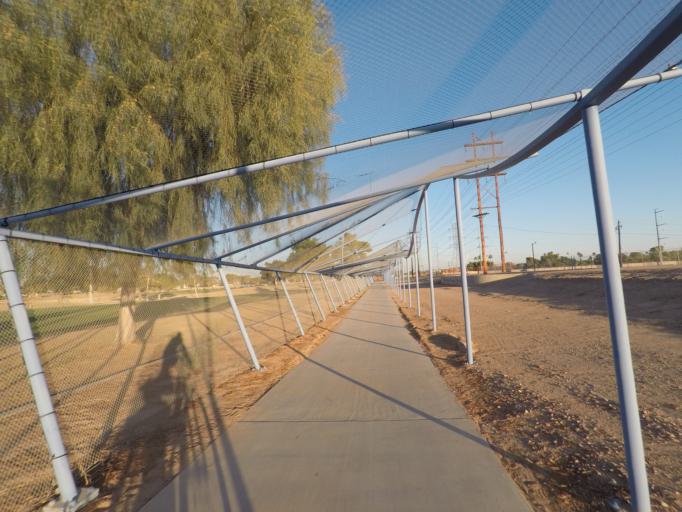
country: US
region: Arizona
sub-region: Maricopa County
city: Guadalupe
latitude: 33.3570
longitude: -111.9357
